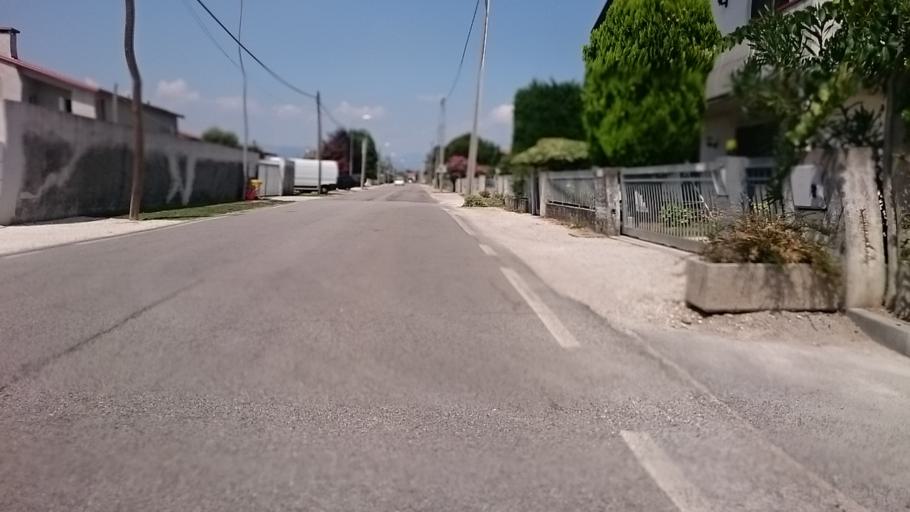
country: IT
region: Veneto
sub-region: Provincia di Padova
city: Fontaniva
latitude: 45.6576
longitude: 11.7575
